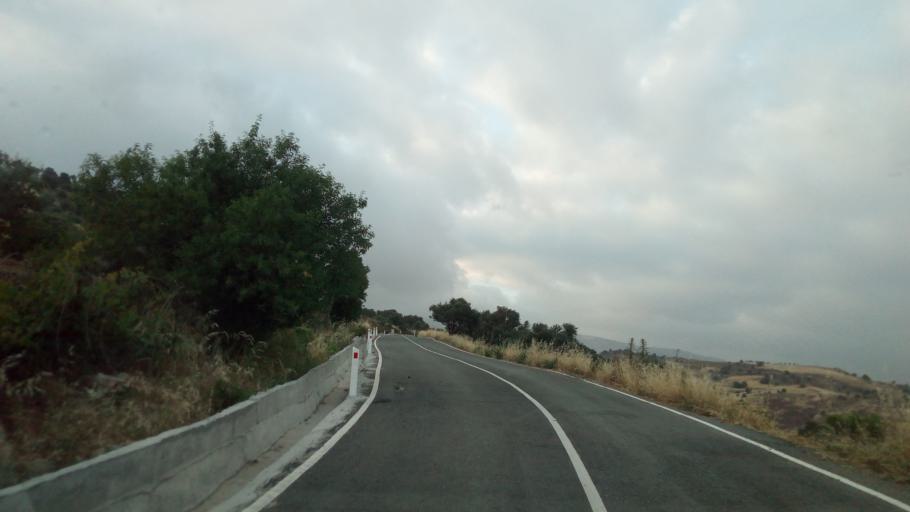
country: CY
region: Limassol
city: Pachna
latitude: 34.8508
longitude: 32.6499
